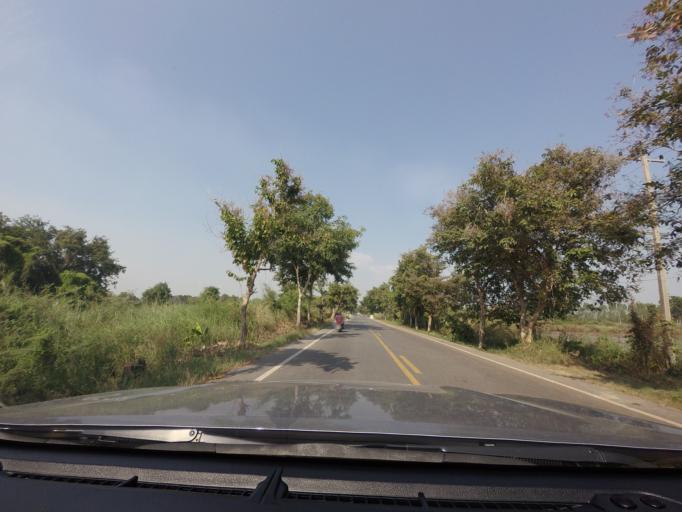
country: TH
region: Sukhothai
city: Kong Krailat
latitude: 16.8718
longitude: 99.9417
